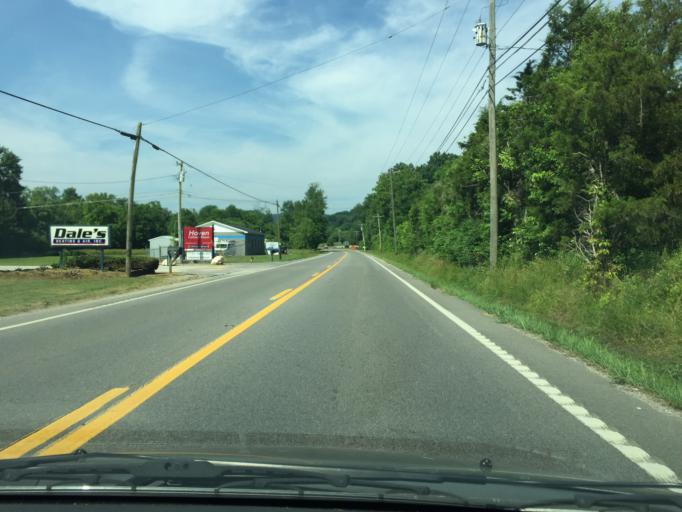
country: US
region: Tennessee
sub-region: Hamilton County
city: Collegedale
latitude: 35.0844
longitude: -85.0244
